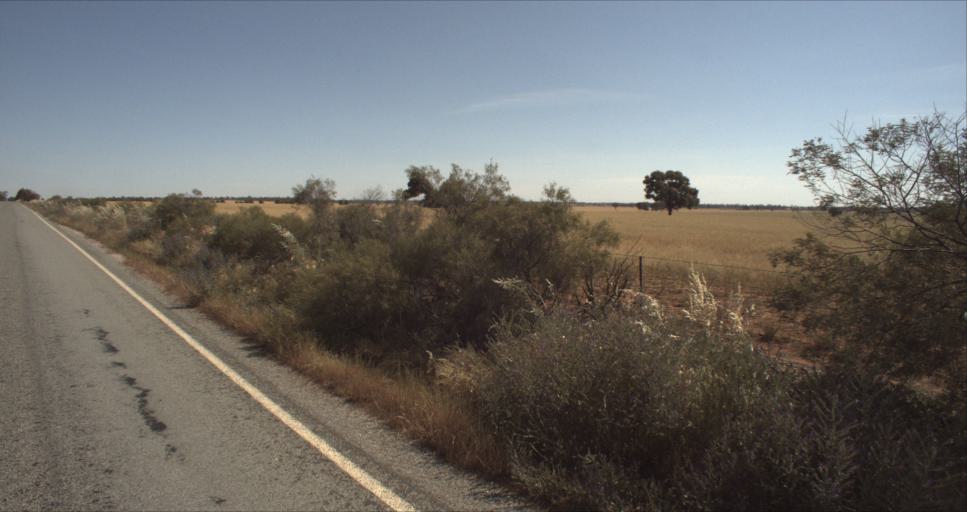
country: AU
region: New South Wales
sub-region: Leeton
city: Leeton
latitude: -34.4583
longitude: 146.4382
